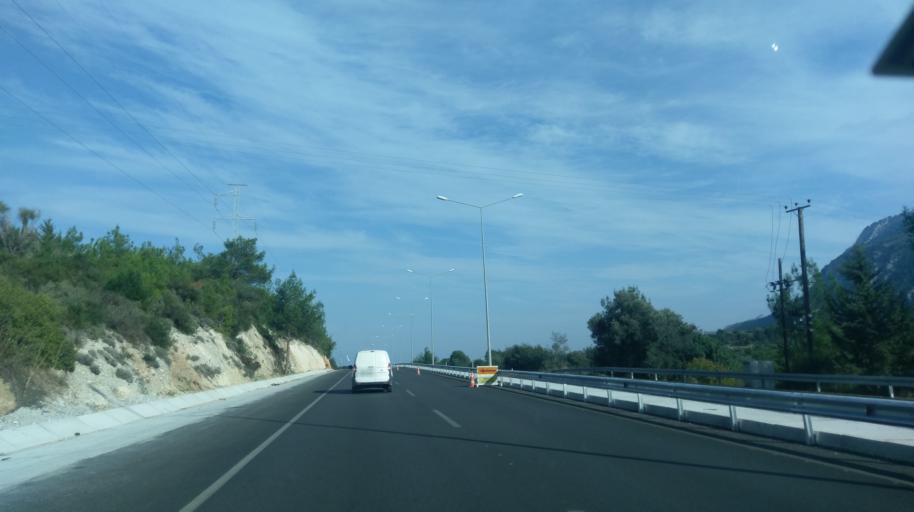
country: CY
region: Keryneia
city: Kyrenia
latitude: 35.3074
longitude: 33.3054
